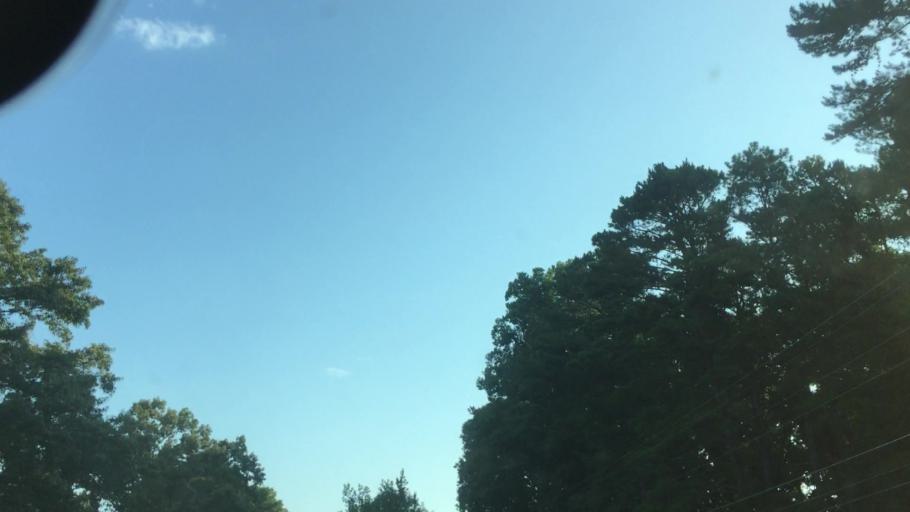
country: US
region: Georgia
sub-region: DeKalb County
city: Pine Mountain
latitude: 33.6744
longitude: -84.1958
